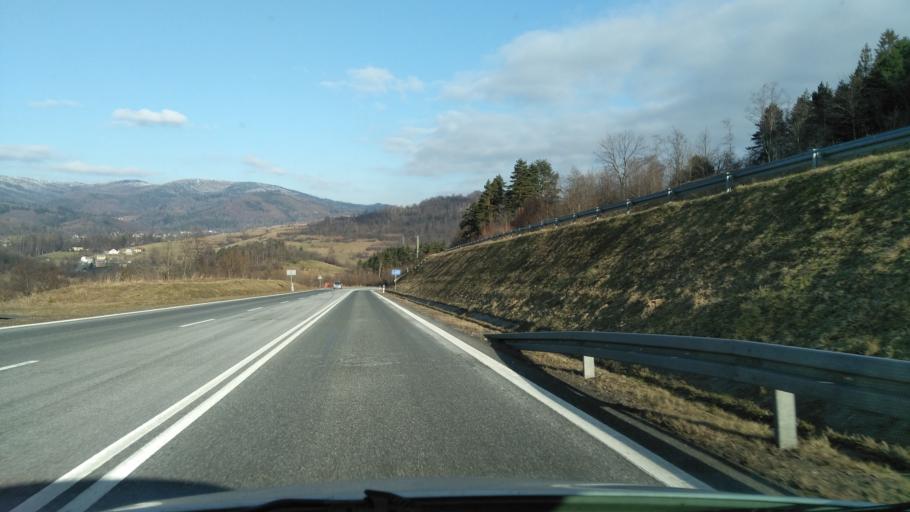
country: PL
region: Silesian Voivodeship
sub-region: Powiat zywiecki
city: Milowka
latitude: 49.5598
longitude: 19.0621
